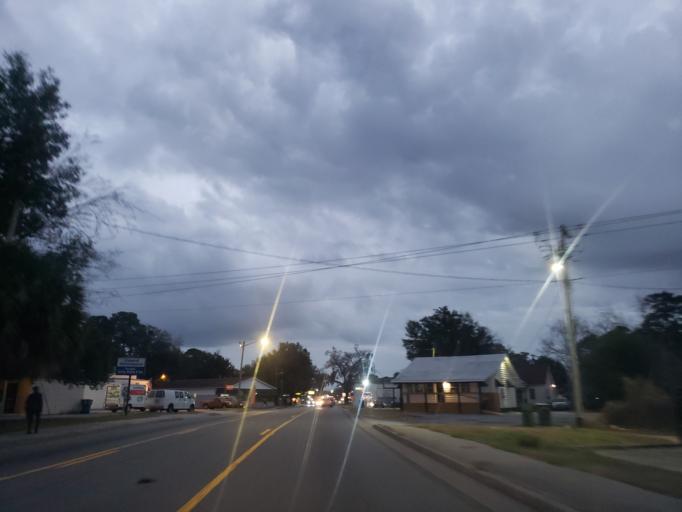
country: US
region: Georgia
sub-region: Chatham County
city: Thunderbolt
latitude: 32.0469
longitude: -81.0644
